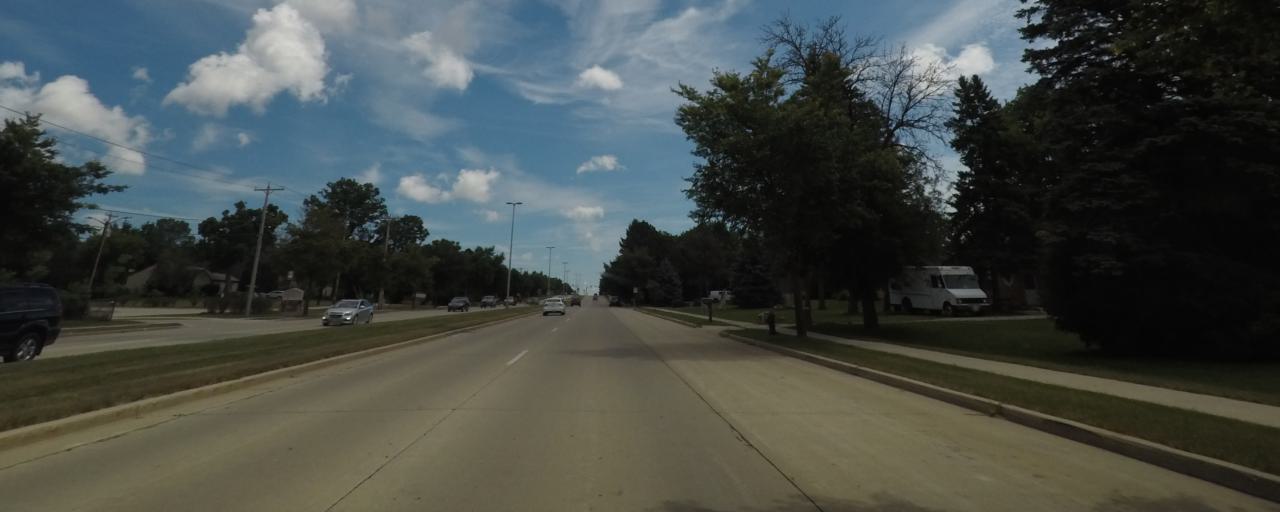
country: US
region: Wisconsin
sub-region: Milwaukee County
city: Greenfield
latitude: 42.9591
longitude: -88.0342
